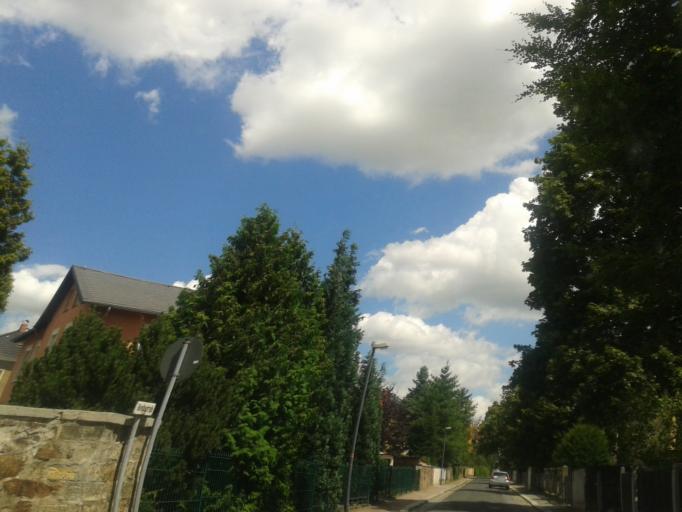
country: DE
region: Saxony
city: Radebeul
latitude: 51.1032
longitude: 13.6810
